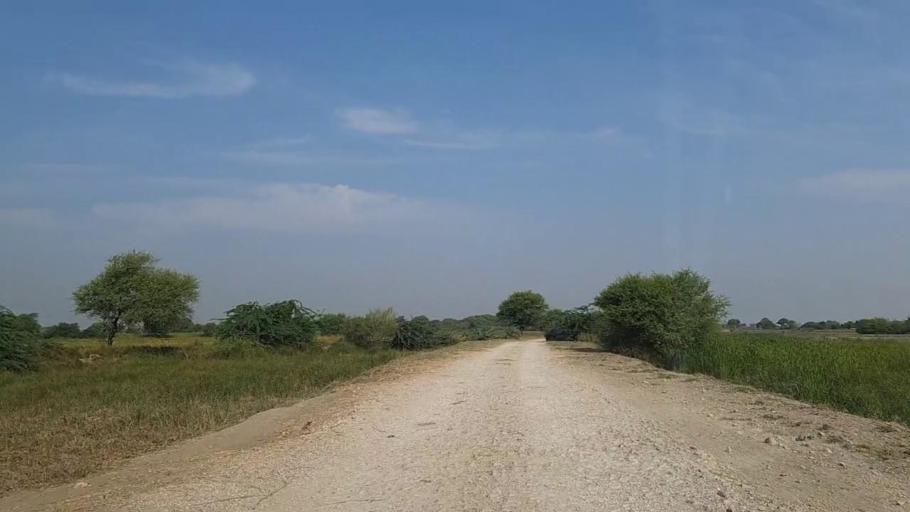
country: PK
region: Sindh
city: Mirpur Batoro
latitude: 24.7144
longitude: 68.2230
